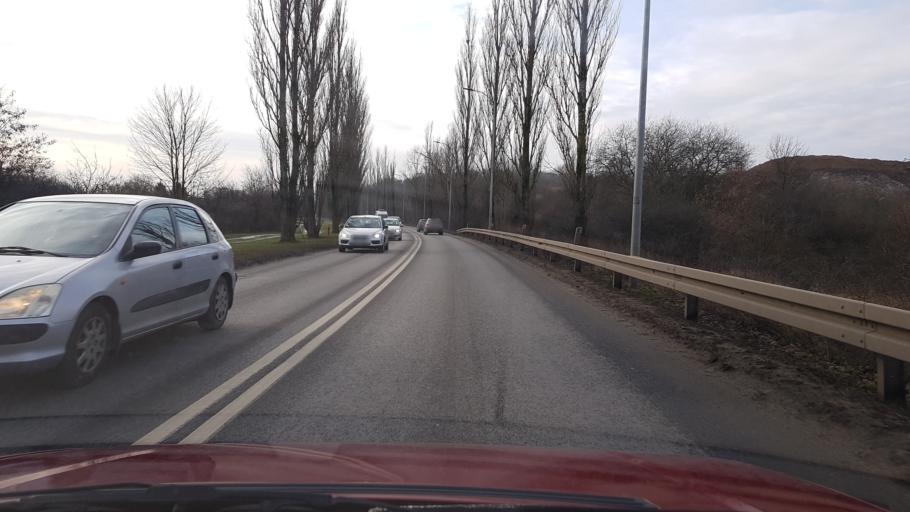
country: PL
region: West Pomeranian Voivodeship
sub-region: Szczecin
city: Szczecin
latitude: 53.4706
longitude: 14.5808
